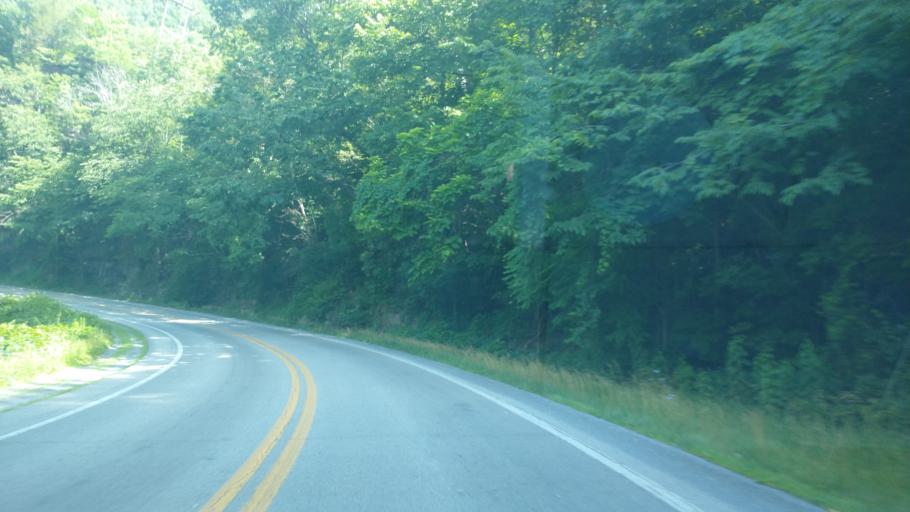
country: US
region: West Virginia
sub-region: McDowell County
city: Welch
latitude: 37.4297
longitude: -81.5053
